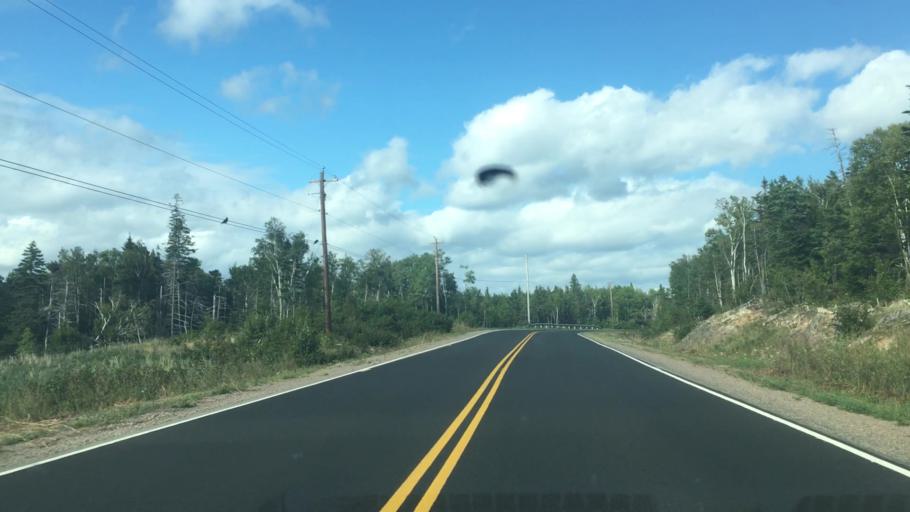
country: CA
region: Nova Scotia
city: Princeville
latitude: 45.8100
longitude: -60.7073
